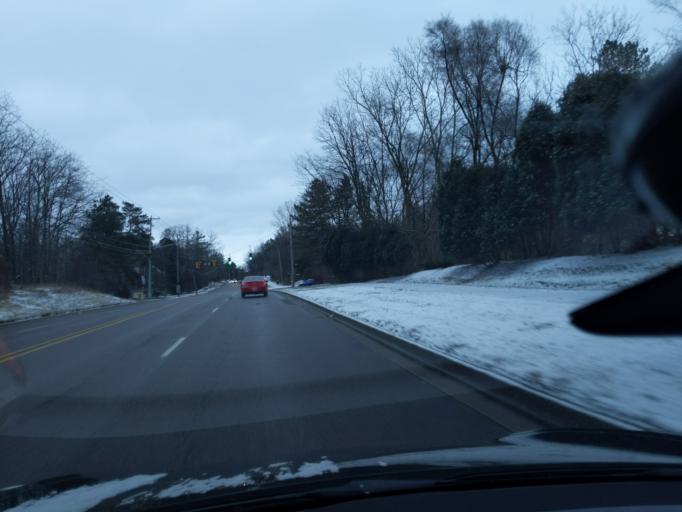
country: US
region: Michigan
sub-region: Ingham County
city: Okemos
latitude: 42.7119
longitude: -84.4467
